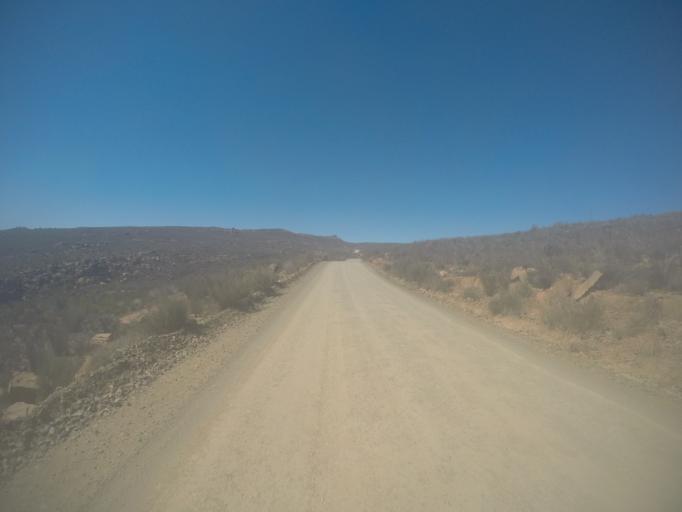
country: ZA
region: Western Cape
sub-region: West Coast District Municipality
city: Clanwilliam
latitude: -32.5045
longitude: 19.2819
